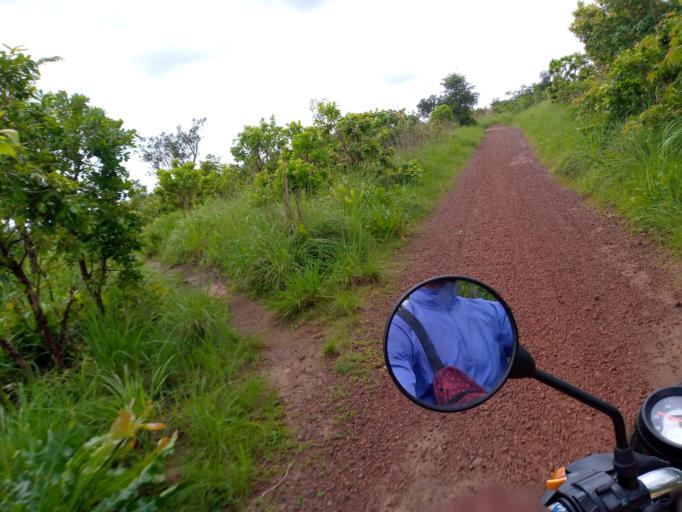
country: SL
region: Northern Province
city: Mange
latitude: 8.9834
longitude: -12.7301
